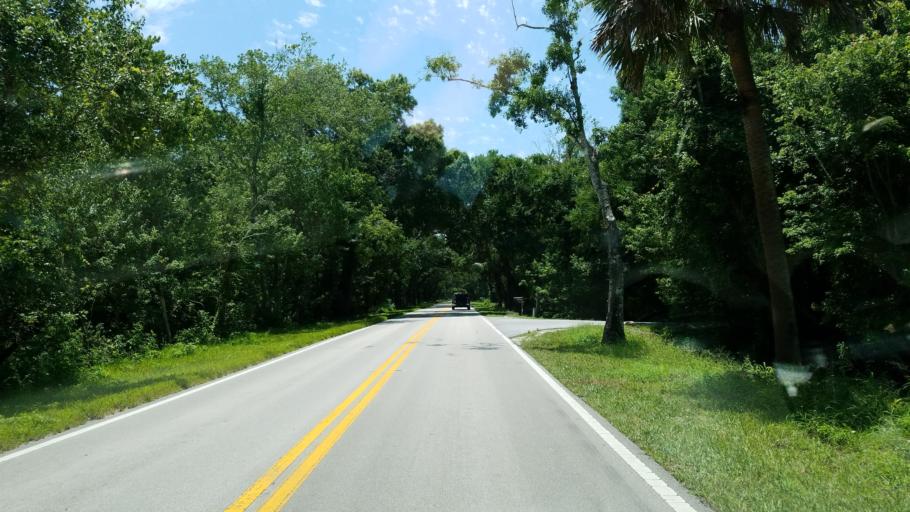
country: US
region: Florida
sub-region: Martin County
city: Indiantown
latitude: 27.1621
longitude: -80.5568
